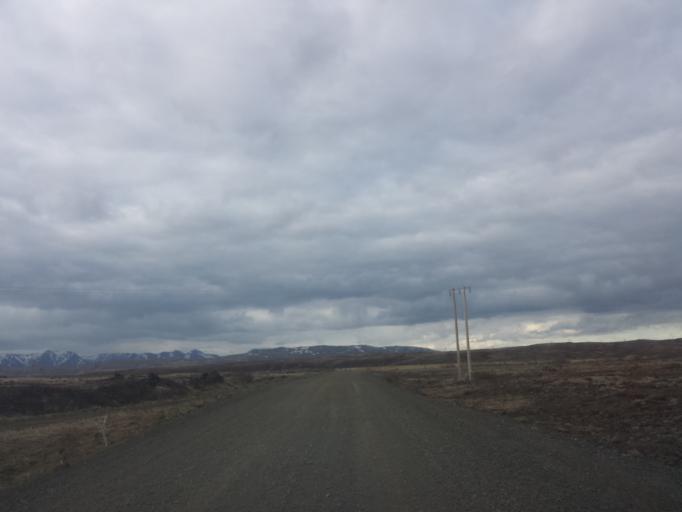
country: IS
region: Capital Region
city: Mosfellsbaer
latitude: 64.0742
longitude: -21.6517
